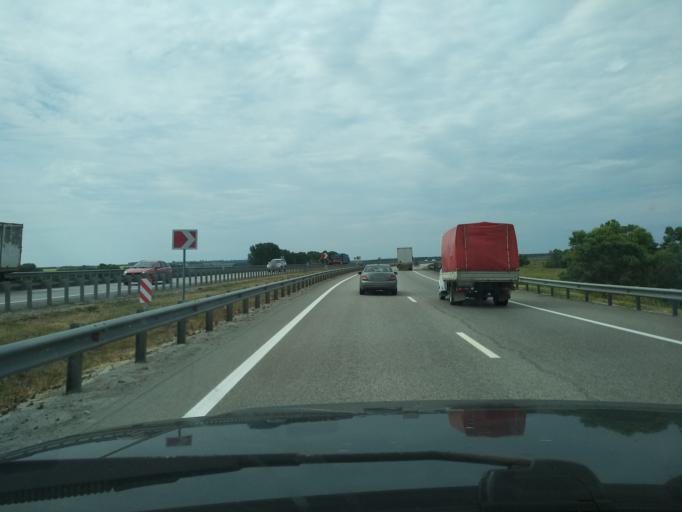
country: RU
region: Lipetsk
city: Khlevnoye
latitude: 52.0614
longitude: 39.1821
